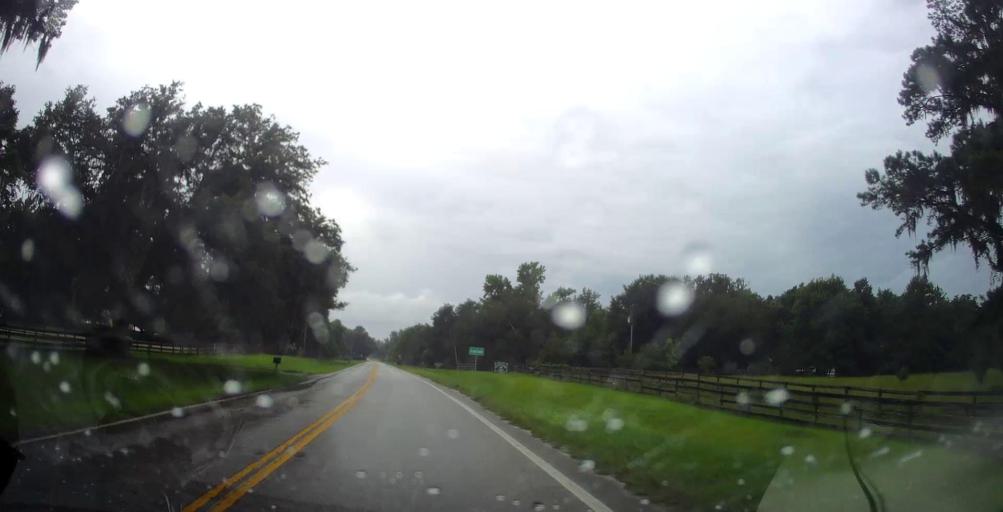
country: US
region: Florida
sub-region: Marion County
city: Citra
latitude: 29.3697
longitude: -82.2510
